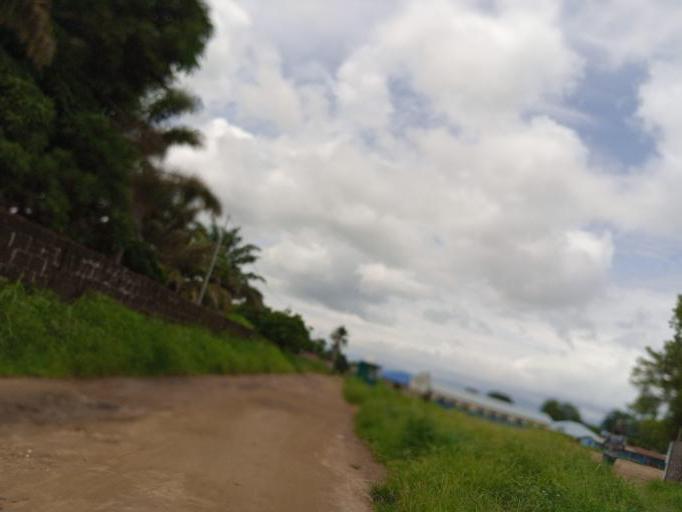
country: SL
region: Northern Province
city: Masoyila
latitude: 8.5992
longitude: -13.1848
